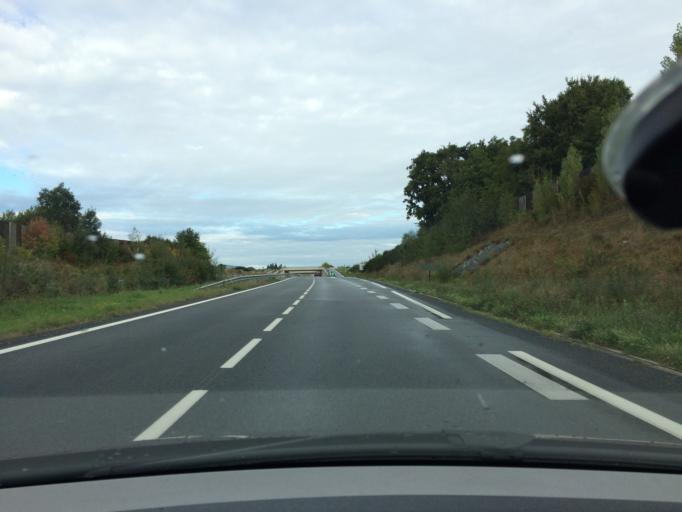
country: FR
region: Brittany
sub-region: Departement d'Ille-et-Vilaine
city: Janze
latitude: 47.9685
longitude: -1.5318
